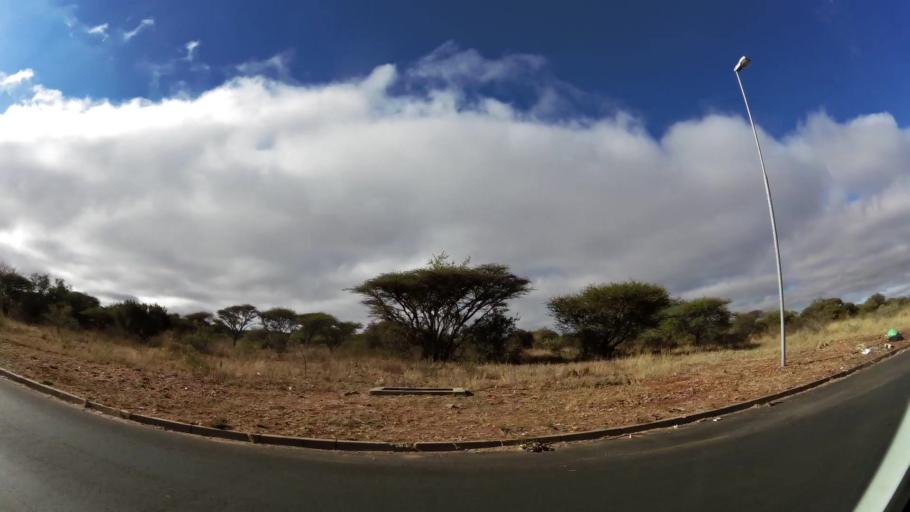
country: ZA
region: Limpopo
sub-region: Capricorn District Municipality
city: Polokwane
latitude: -23.9206
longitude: 29.4761
